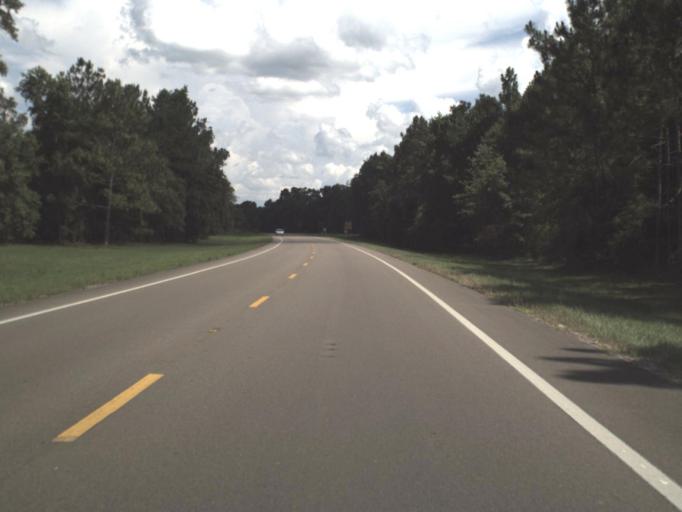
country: US
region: Florida
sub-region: Alachua County
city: High Springs
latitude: 29.8478
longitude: -82.6079
